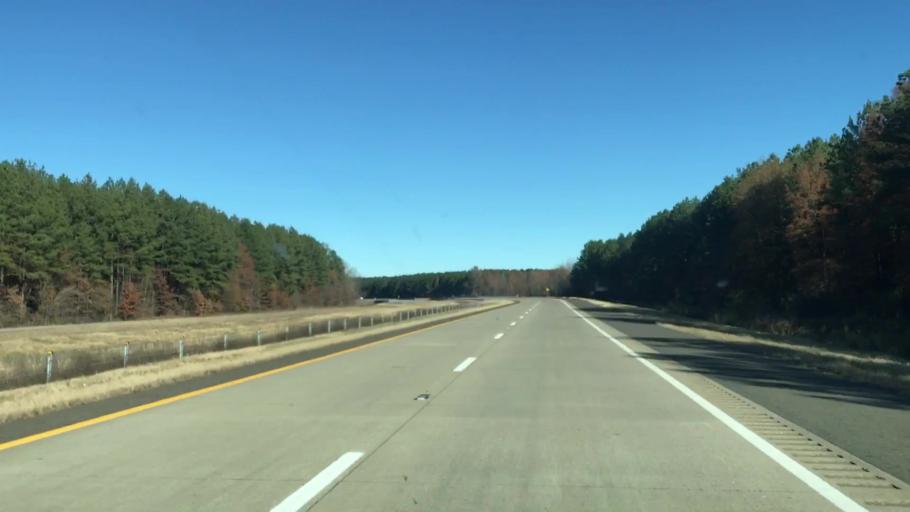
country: US
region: Texas
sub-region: Bowie County
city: Texarkana
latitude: 33.2367
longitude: -93.8730
